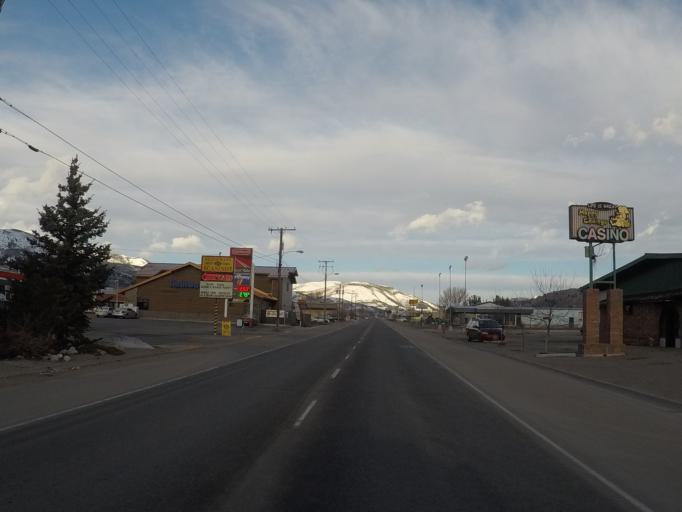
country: US
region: Montana
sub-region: Deer Lodge County
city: Anaconda
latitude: 46.1268
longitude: -112.9320
